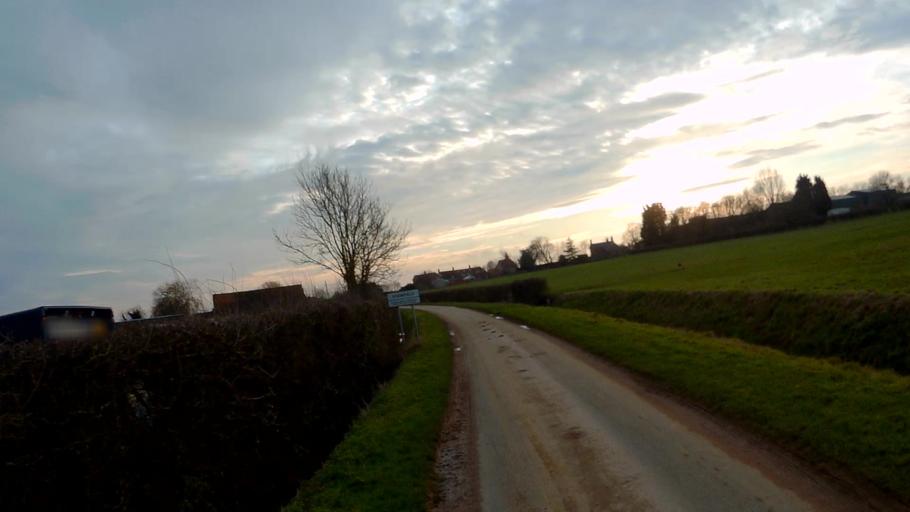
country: GB
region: England
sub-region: Lincolnshire
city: Bourne
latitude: 52.8146
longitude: -0.3988
